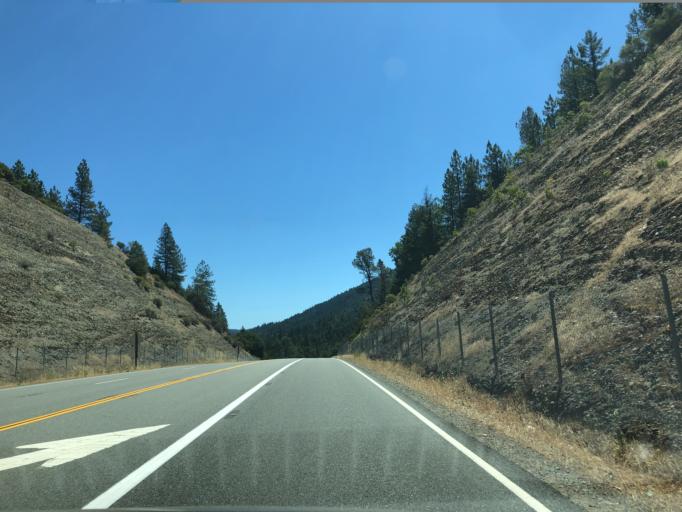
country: US
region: California
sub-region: Trinity County
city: Lewiston
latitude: 40.6729
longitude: -122.8778
